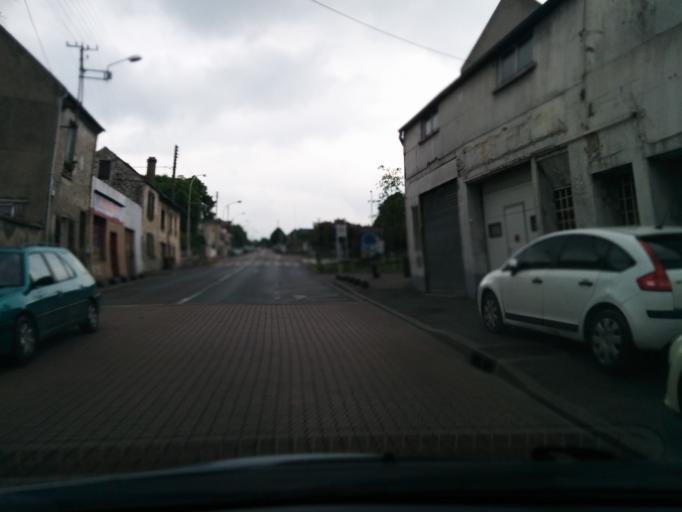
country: FR
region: Ile-de-France
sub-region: Departement des Yvelines
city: Limay
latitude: 48.9958
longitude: 1.7332
